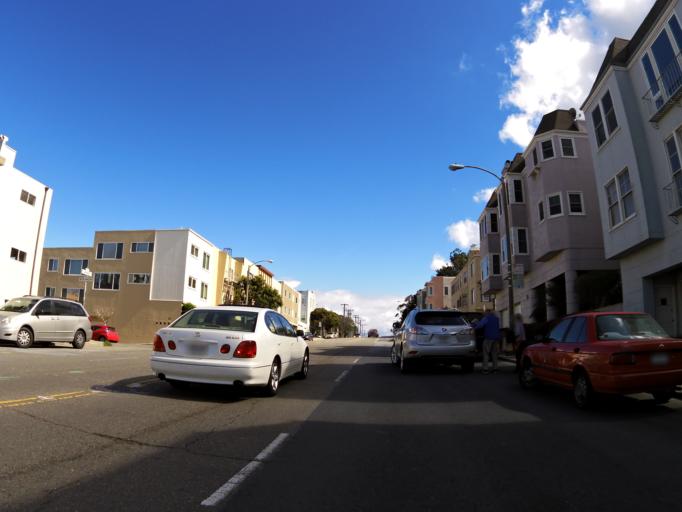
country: US
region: California
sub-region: San Francisco County
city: San Francisco
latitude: 37.7800
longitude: -122.4553
